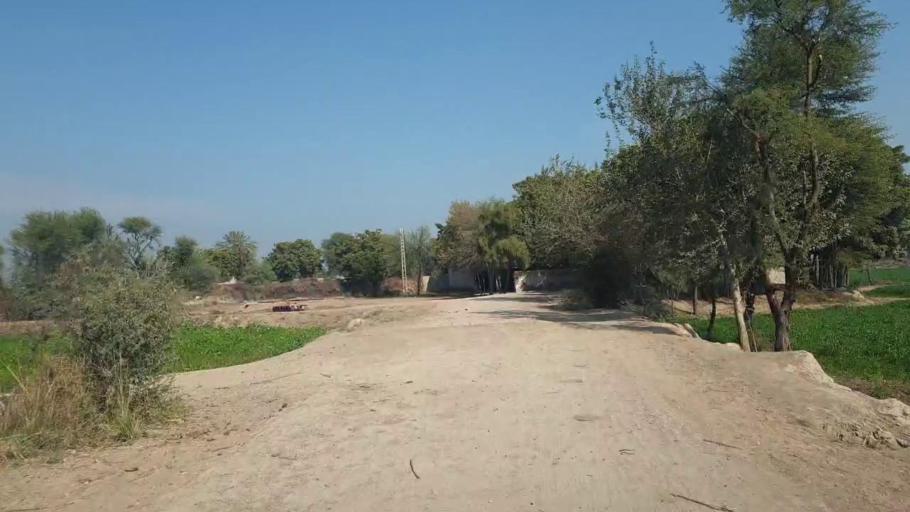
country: PK
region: Sindh
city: Shahdadpur
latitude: 25.9884
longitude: 68.5169
